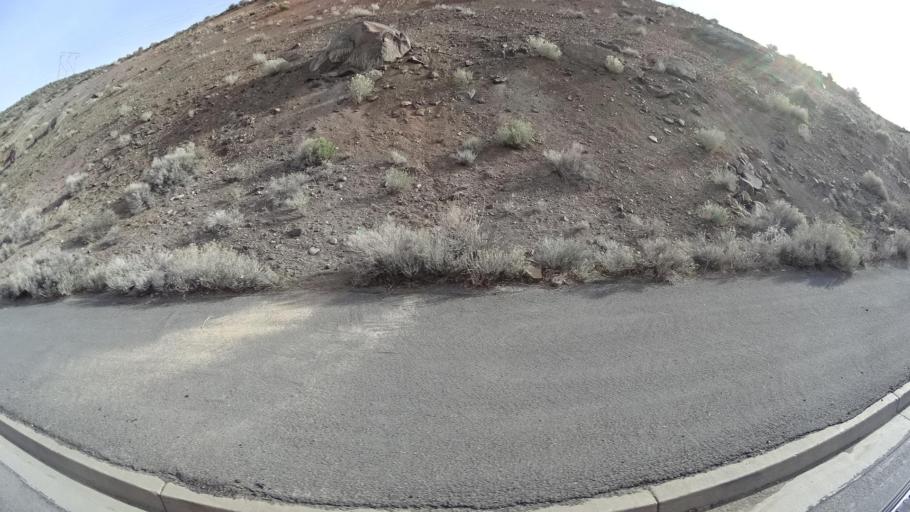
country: US
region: Nevada
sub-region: Washoe County
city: Mogul
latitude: 39.5141
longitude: -119.9501
